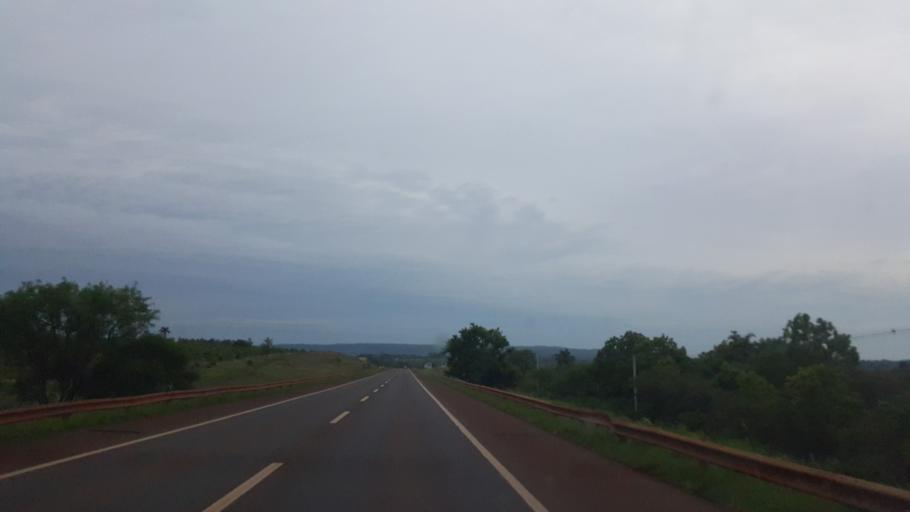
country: AR
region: Misiones
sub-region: Departamento de Apostoles
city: San Jose
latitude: -27.7731
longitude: -55.8069
